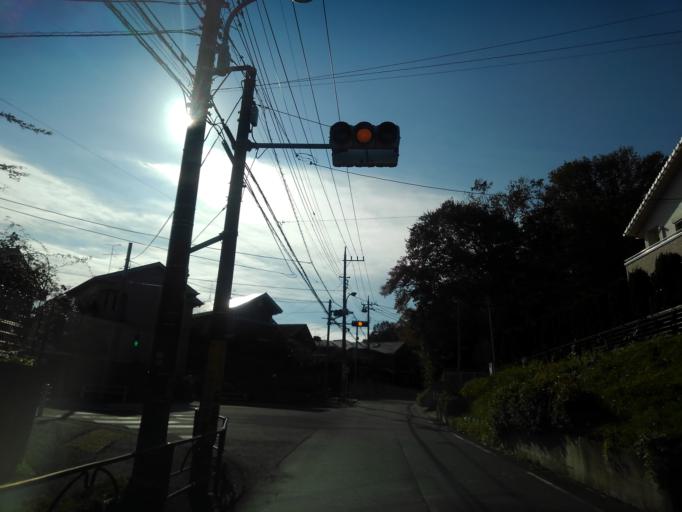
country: JP
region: Tokyo
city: Hachioji
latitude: 35.6886
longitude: 139.3517
